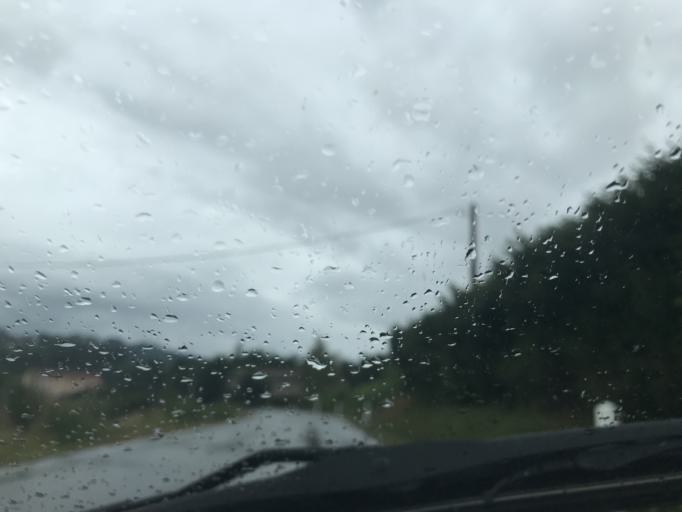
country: FR
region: Auvergne
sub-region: Departement du Puy-de-Dome
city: Ambert
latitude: 45.5813
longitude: 3.7349
